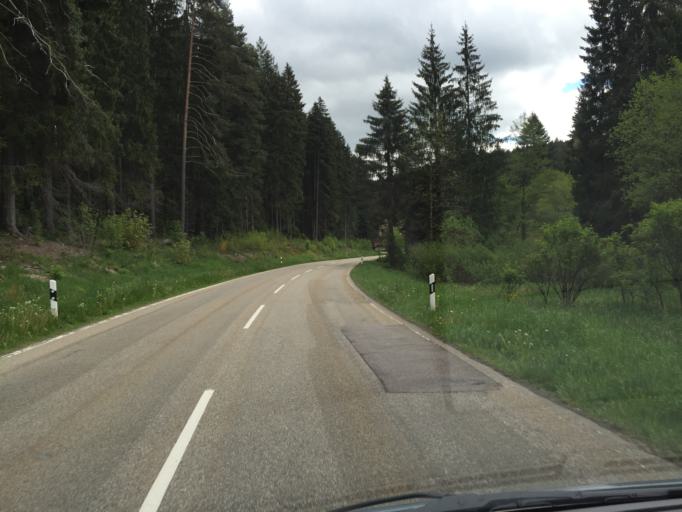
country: DE
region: Baden-Wuerttemberg
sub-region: Freiburg Region
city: Unterkirnach
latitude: 48.0746
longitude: 8.3849
